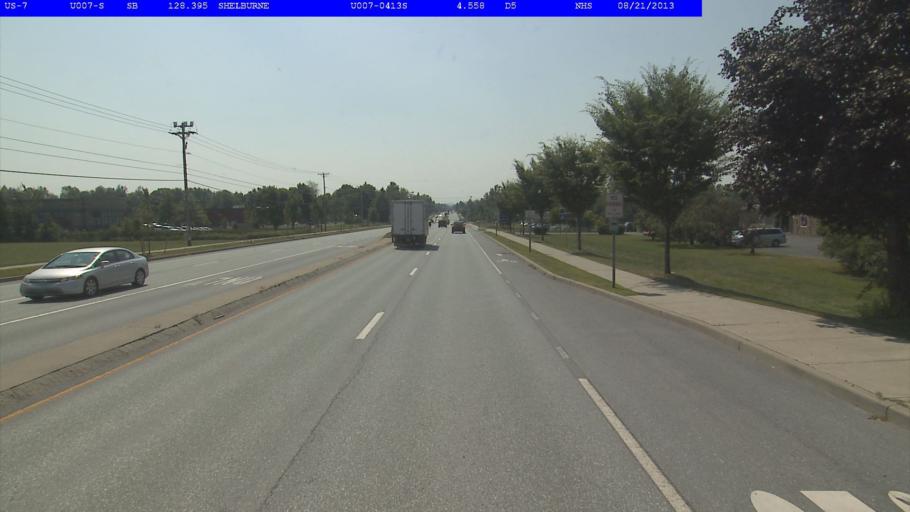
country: US
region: Vermont
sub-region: Chittenden County
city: Burlington
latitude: 44.4086
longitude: -73.2160
